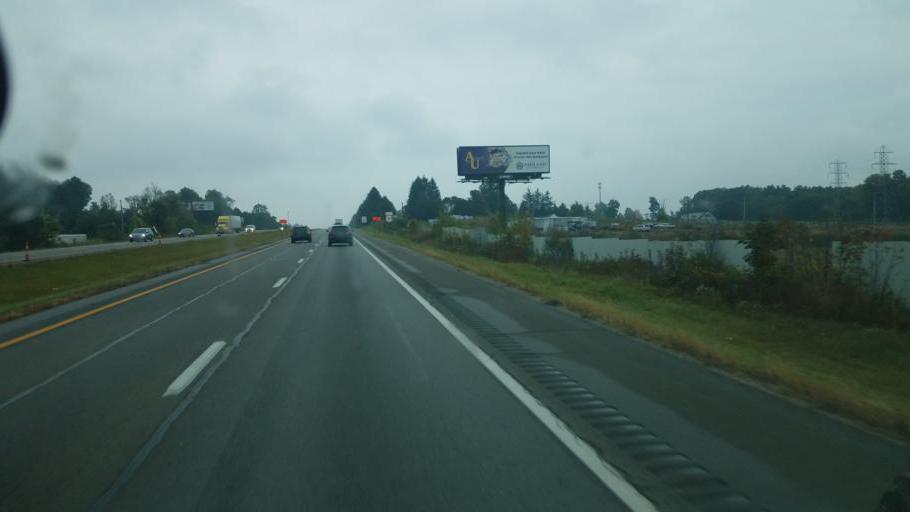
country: US
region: Ohio
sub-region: Richland County
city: Lincoln Heights
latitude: 40.7790
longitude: -82.4877
